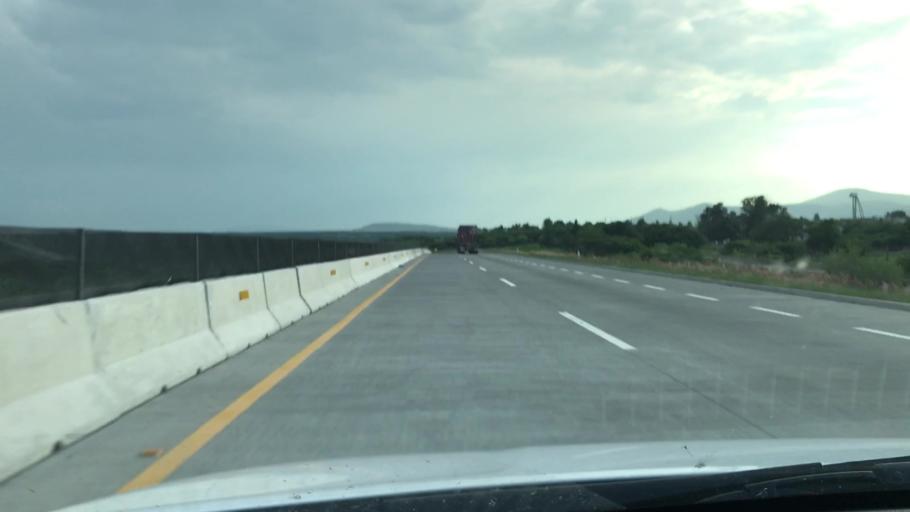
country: MX
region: Jalisco
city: Degollado
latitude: 20.3853
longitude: -102.1150
